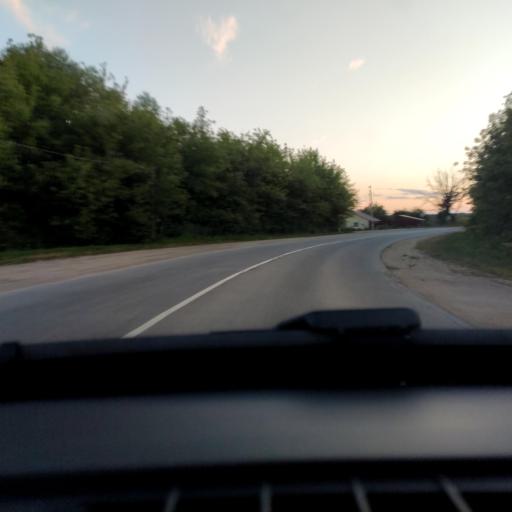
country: RU
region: Lipetsk
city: Zadonsk
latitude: 52.2965
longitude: 38.8492
